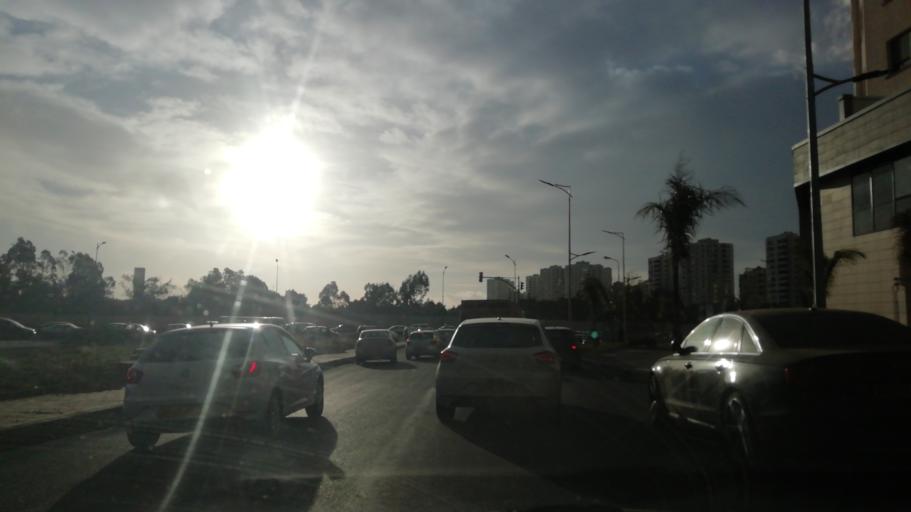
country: DZ
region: Oran
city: Bir el Djir
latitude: 35.7120
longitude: -0.5748
